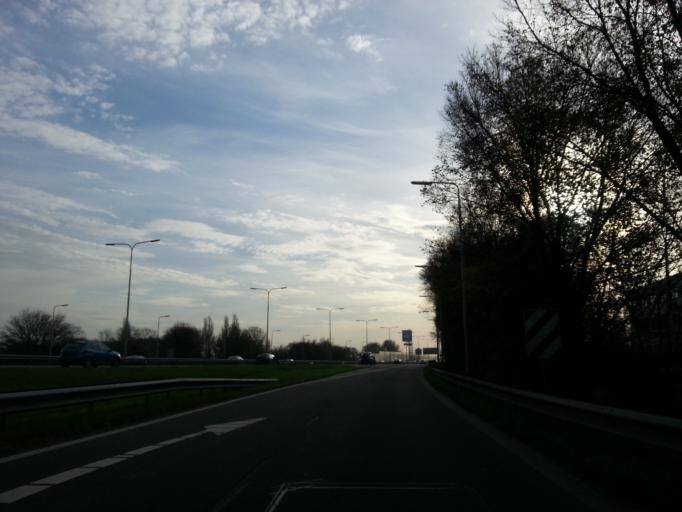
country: NL
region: South Holland
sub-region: Gemeente Delft
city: Delft
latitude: 52.0095
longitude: 4.3793
